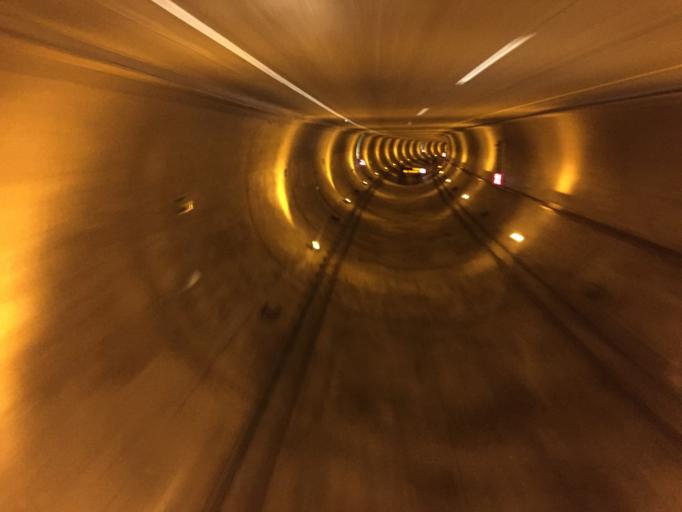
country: MX
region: Puebla
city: Xicotepec de Juarez
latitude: 20.3044
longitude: -97.9676
